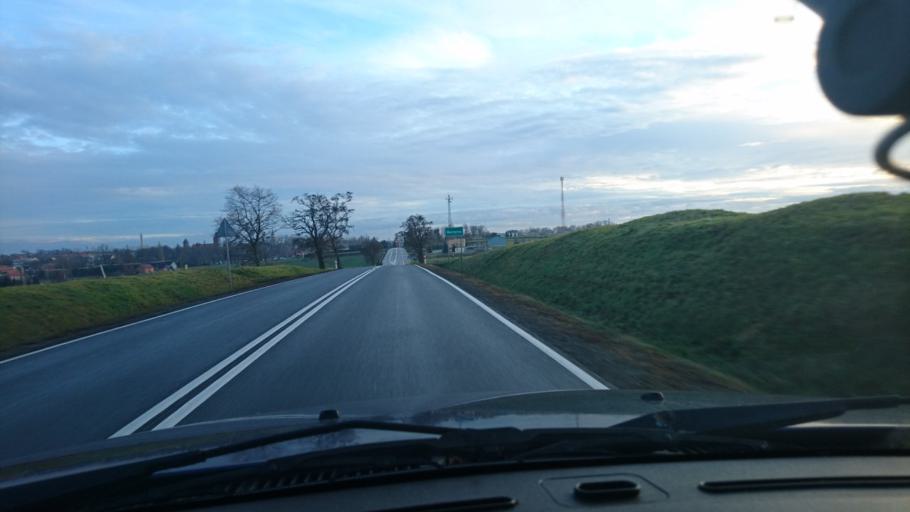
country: PL
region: Opole Voivodeship
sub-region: Powiat kluczborski
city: Byczyna
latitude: 51.1221
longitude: 18.2055
